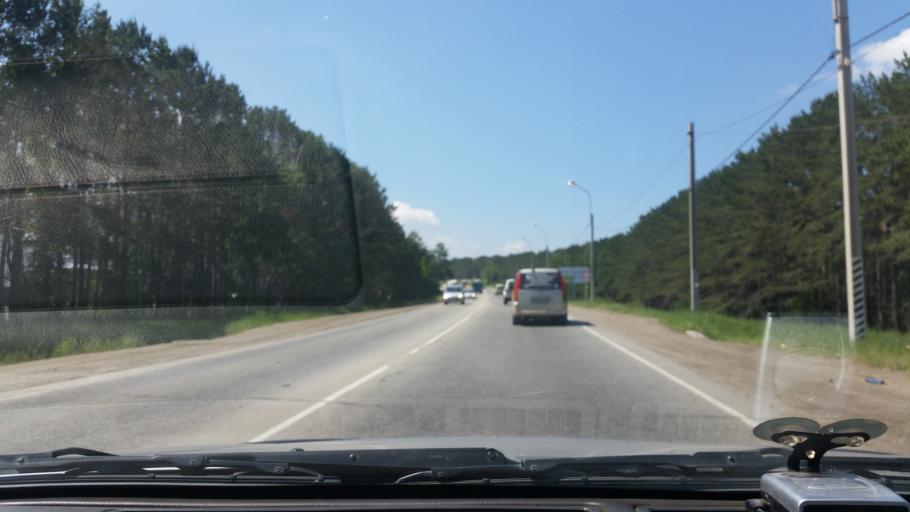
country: RU
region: Irkutsk
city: Smolenshchina
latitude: 52.2591
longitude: 104.1830
